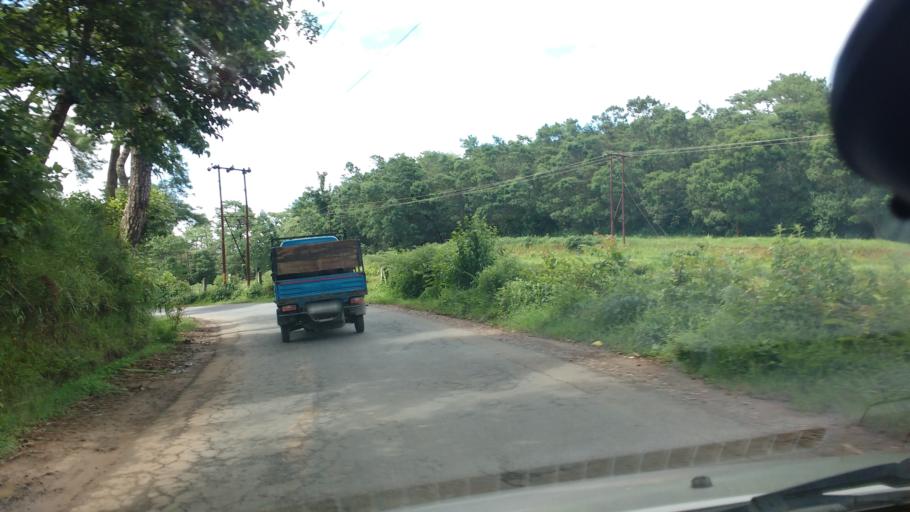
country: IN
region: Meghalaya
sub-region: East Khasi Hills
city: Shillong
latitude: 25.5424
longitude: 91.8477
